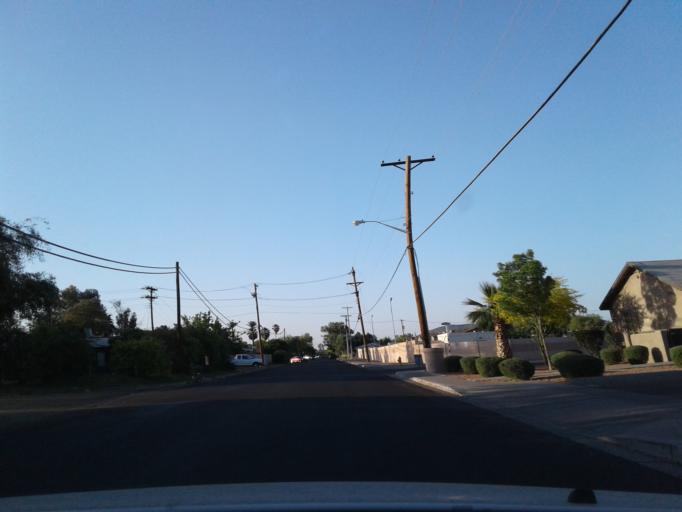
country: US
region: Arizona
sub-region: Maricopa County
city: Glendale
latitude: 33.5478
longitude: -112.1040
